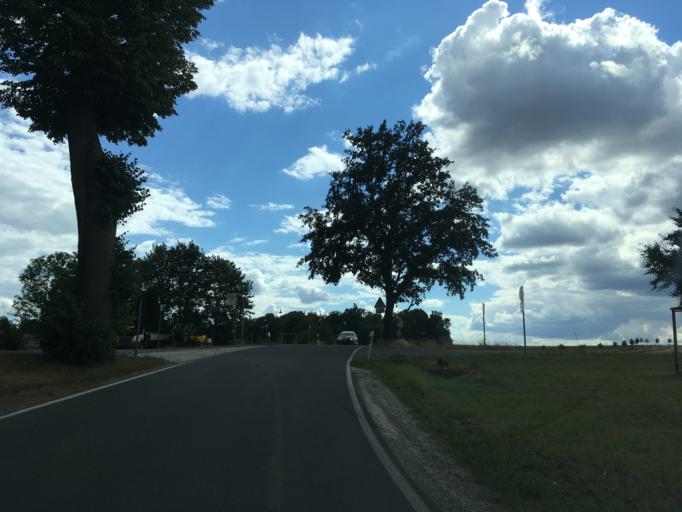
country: DE
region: Saxony
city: Wachau
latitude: 51.1586
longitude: 13.9005
